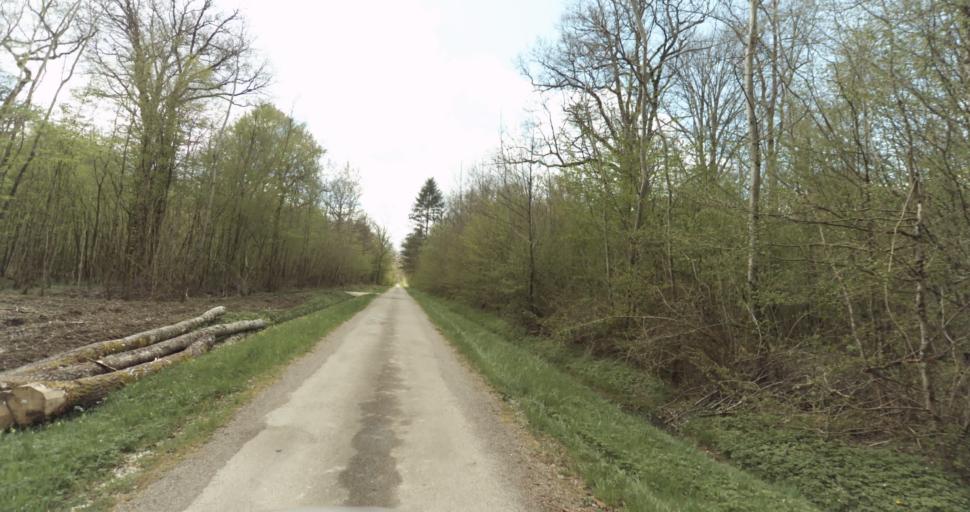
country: FR
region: Franche-Comte
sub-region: Departement du Jura
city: Champvans
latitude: 47.1636
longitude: 5.4441
